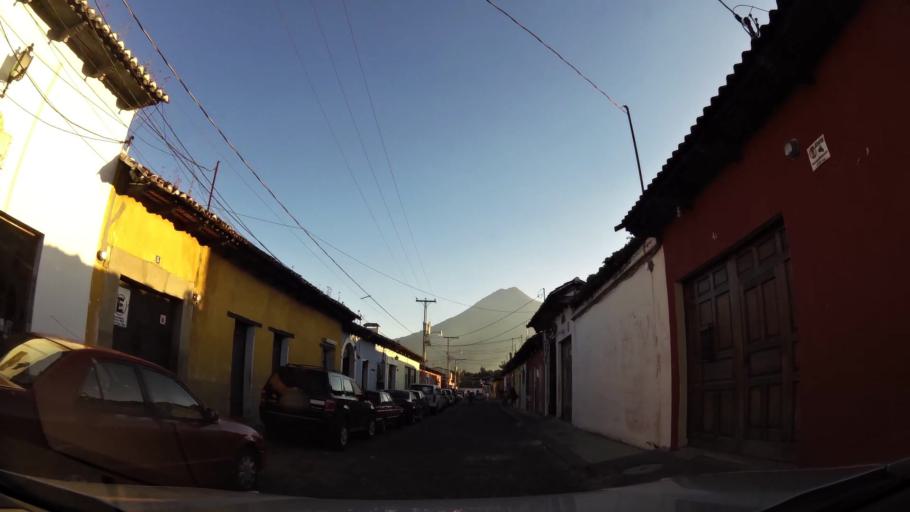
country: GT
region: Sacatepequez
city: Antigua Guatemala
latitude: 14.5559
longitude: -90.7353
